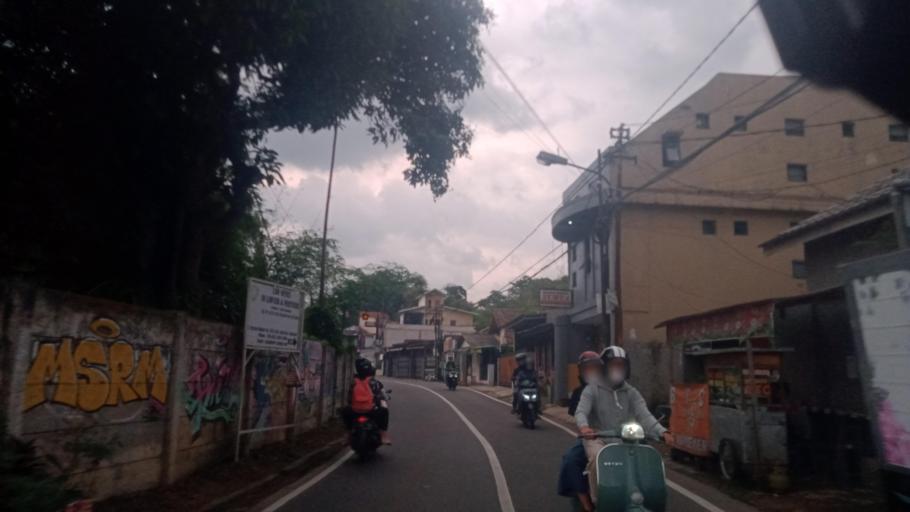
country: ID
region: West Java
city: Lembang
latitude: -6.8535
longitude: 107.5916
